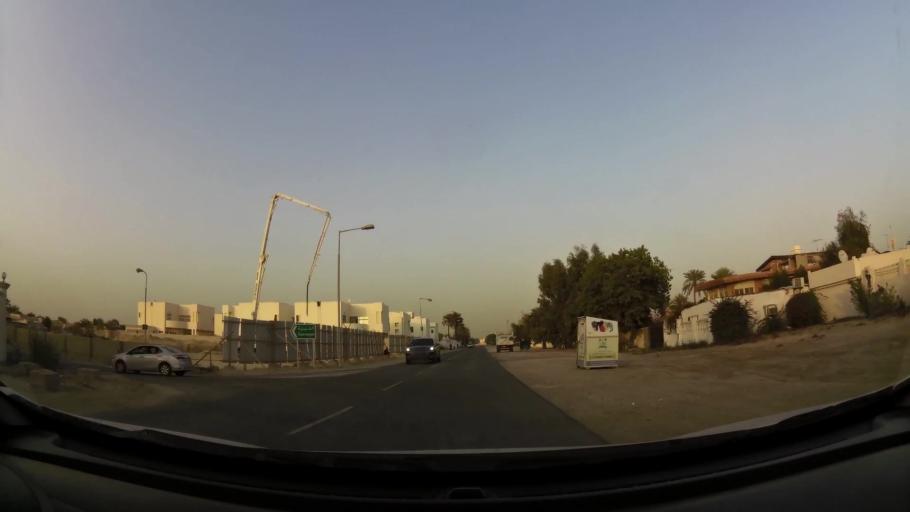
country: BH
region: Northern
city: Madinat `Isa
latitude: 26.1936
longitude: 50.4678
